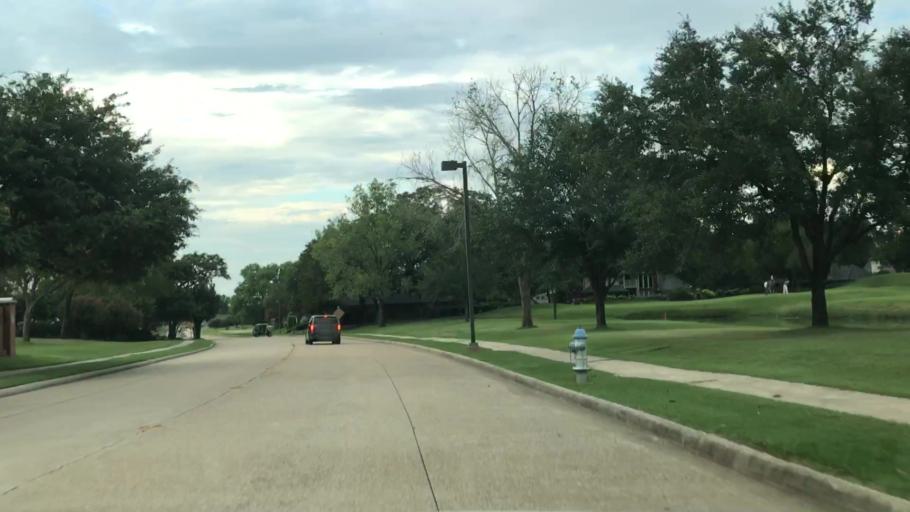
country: US
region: Texas
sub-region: Denton County
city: The Colony
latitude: 33.0364
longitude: -96.8462
